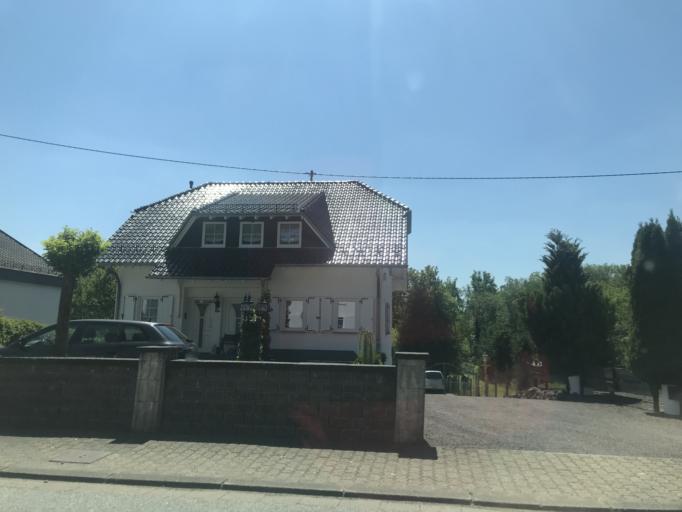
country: DE
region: Saarland
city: Losheim
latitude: 49.4505
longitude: 6.7573
